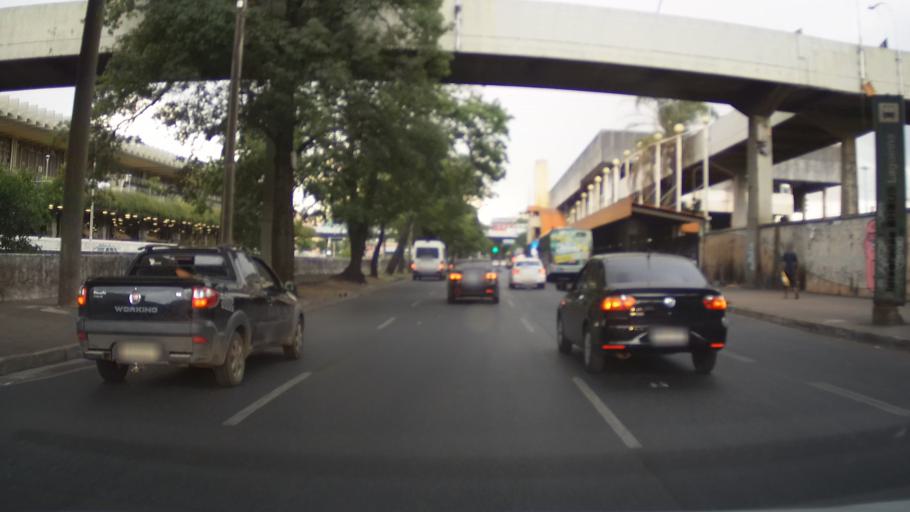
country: BR
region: Minas Gerais
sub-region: Belo Horizonte
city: Belo Horizonte
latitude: -19.9126
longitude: -43.9412
